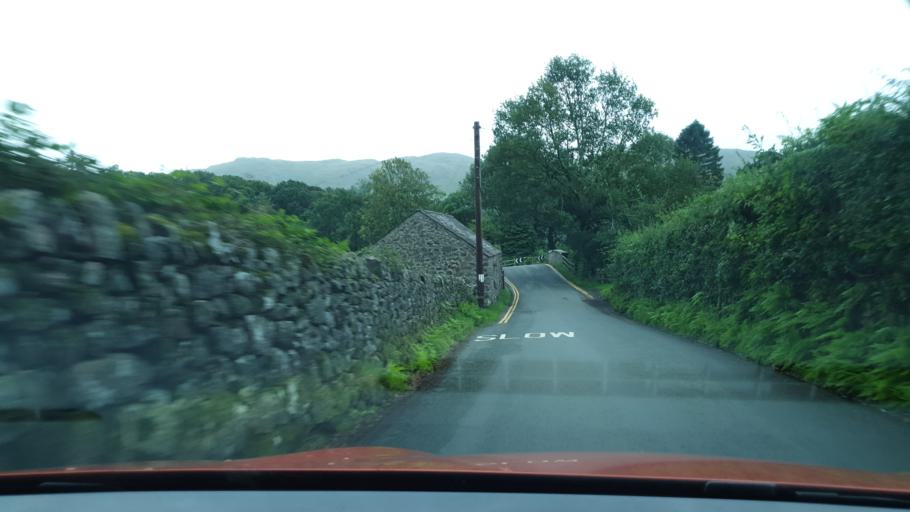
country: GB
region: England
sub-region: Cumbria
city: Seascale
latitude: 54.3877
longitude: -3.3176
